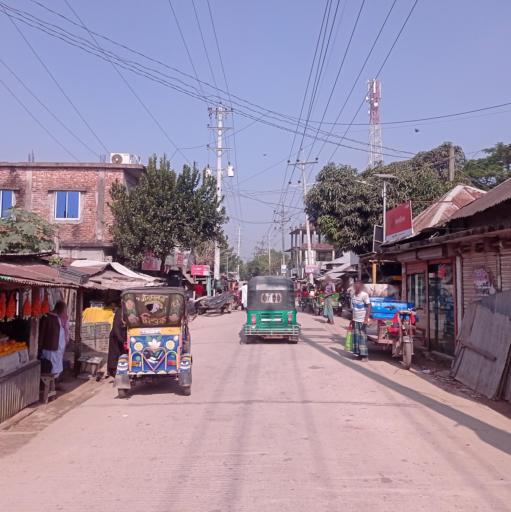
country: BD
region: Dhaka
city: Narsingdi
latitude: 24.0682
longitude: 90.6919
